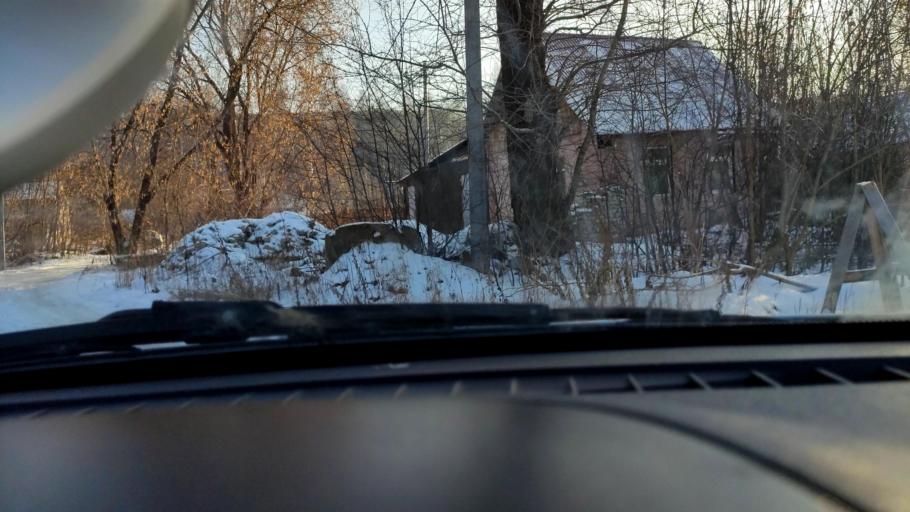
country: RU
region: Perm
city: Perm
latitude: 58.0661
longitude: 56.3385
